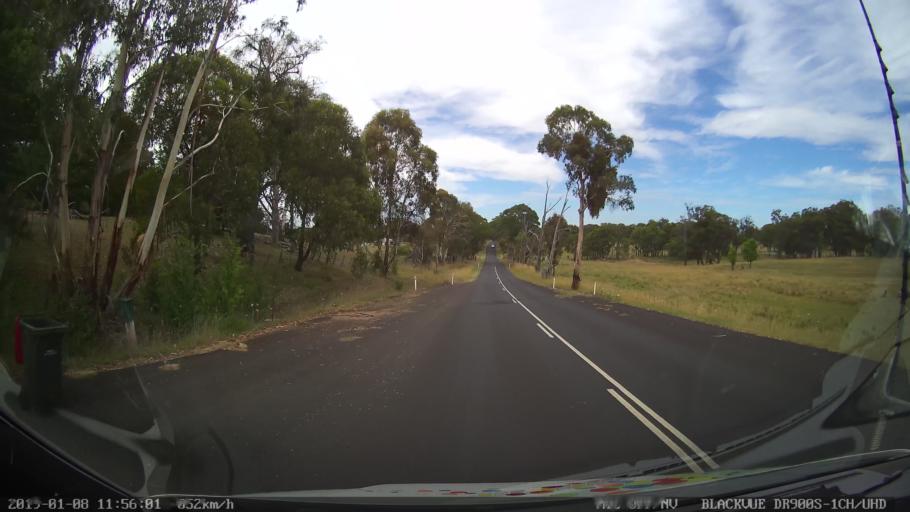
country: AU
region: New South Wales
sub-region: Armidale Dumaresq
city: Armidale
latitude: -30.4356
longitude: 151.5650
